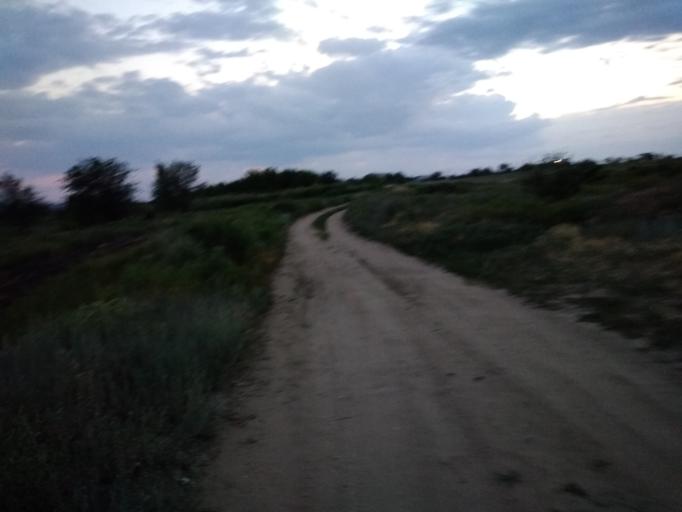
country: RU
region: Volgograd
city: Vodstroy
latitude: 48.8034
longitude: 44.5390
